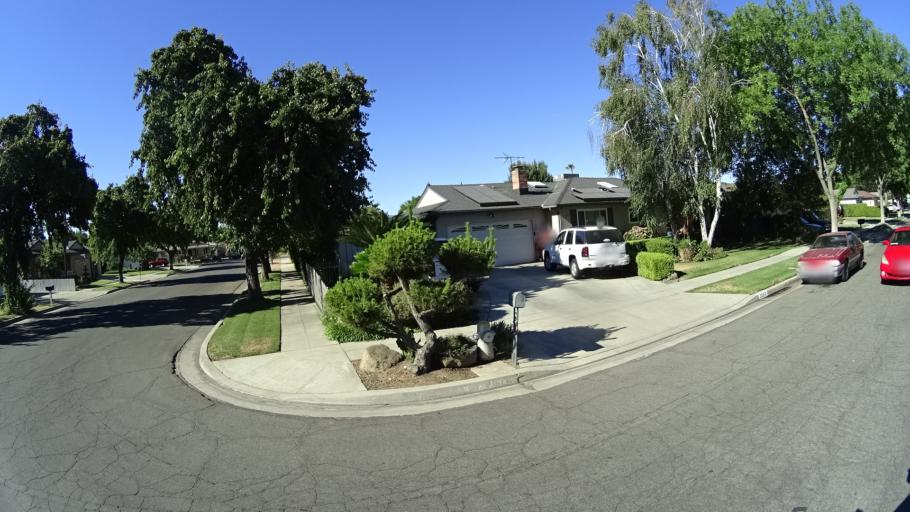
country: US
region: California
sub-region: Fresno County
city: Fresno
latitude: 36.8043
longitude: -119.8405
